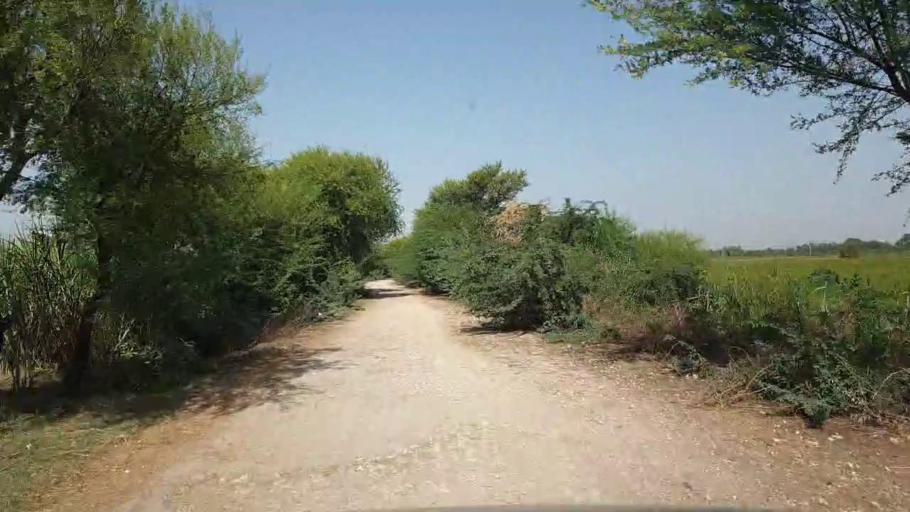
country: PK
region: Sindh
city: Tando Bago
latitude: 24.7589
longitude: 69.0243
